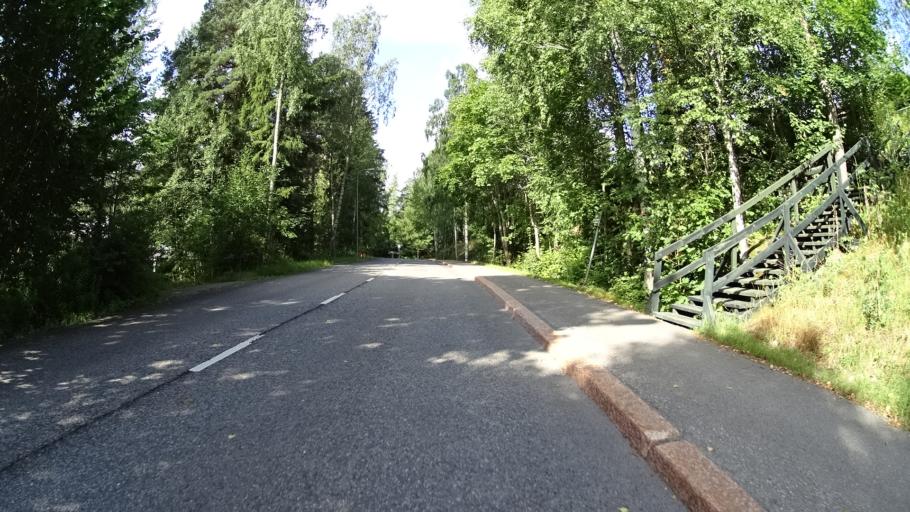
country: FI
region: Uusimaa
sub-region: Helsinki
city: Kauniainen
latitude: 60.2082
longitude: 24.6989
